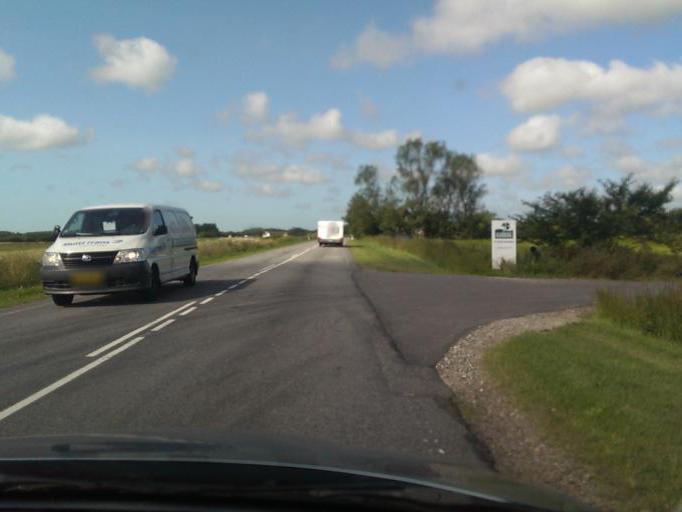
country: DK
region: North Denmark
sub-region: Alborg Kommune
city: Vadum
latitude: 57.2059
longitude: 9.8754
